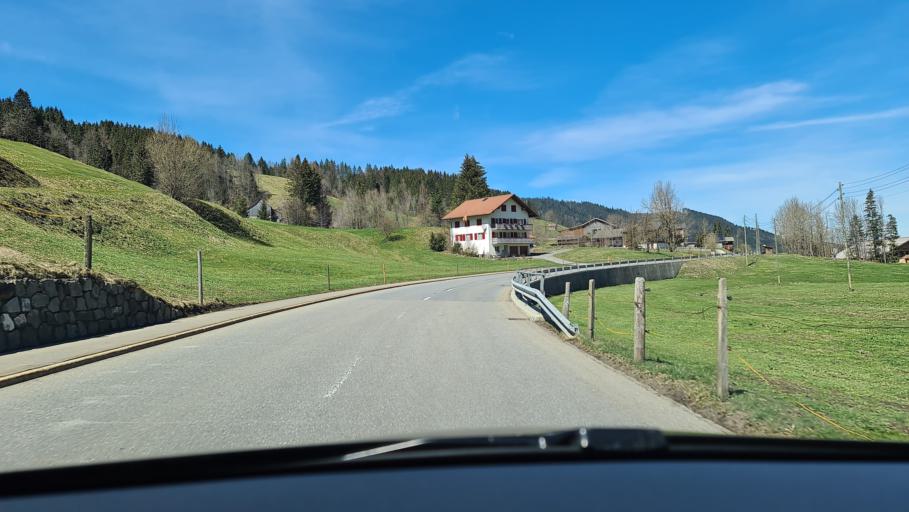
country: CH
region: Schwyz
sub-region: Bezirk Schwyz
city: Rothenthurm
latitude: 47.0847
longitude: 8.7219
